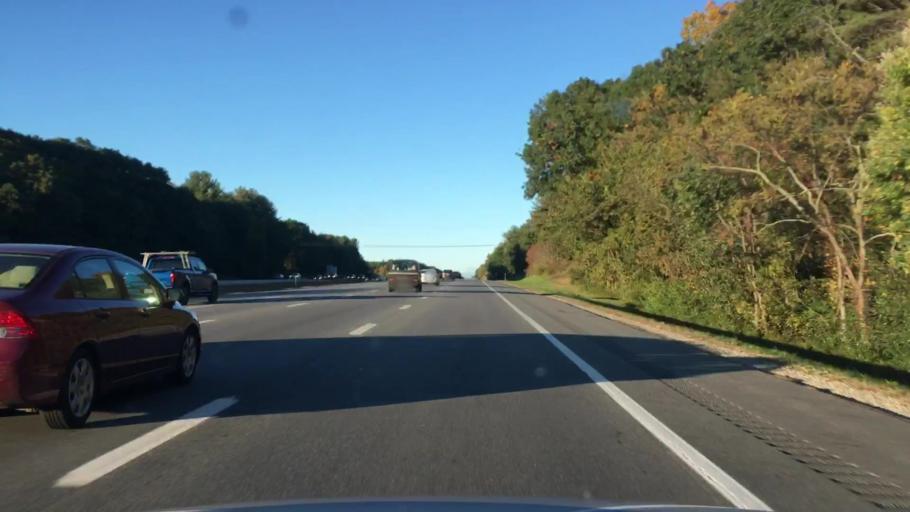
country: US
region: New Hampshire
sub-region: Rockingham County
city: North Hampton
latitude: 43.0019
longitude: -70.8429
